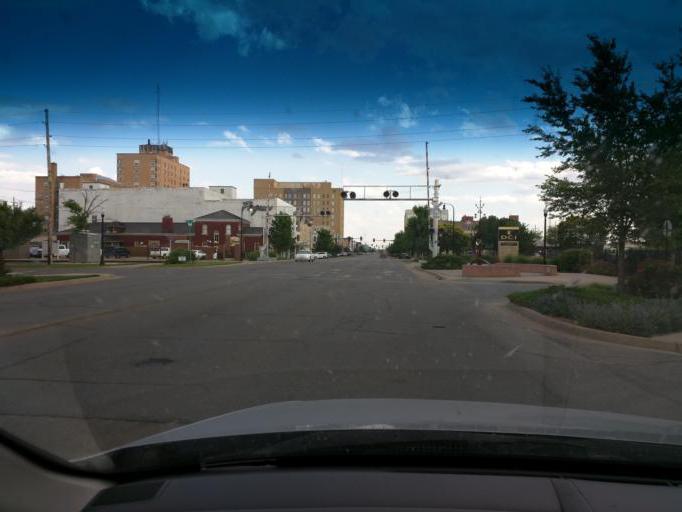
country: US
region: Kansas
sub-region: Reno County
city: Hutchinson
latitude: 38.0565
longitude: -97.9318
